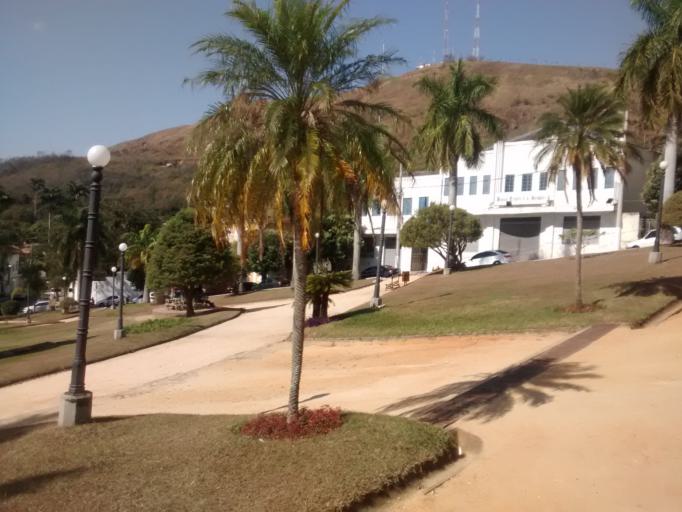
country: BR
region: Rio de Janeiro
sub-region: Vassouras
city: Vassouras
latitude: -22.4096
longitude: -43.6613
